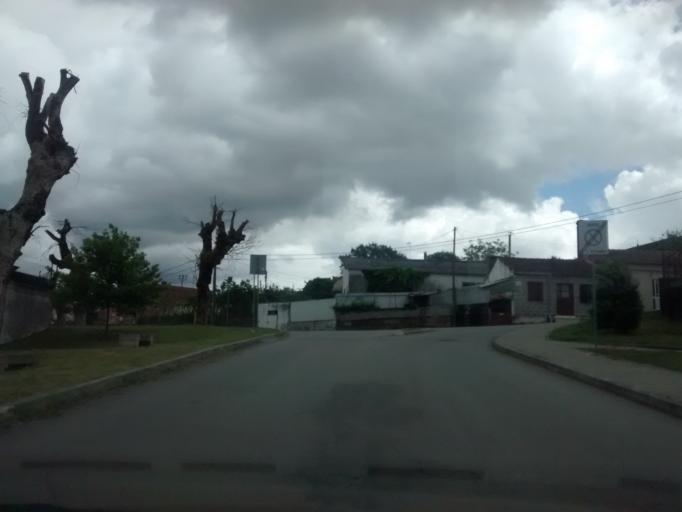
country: PT
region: Braga
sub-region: Braga
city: Braga
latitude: 41.5705
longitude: -8.4353
